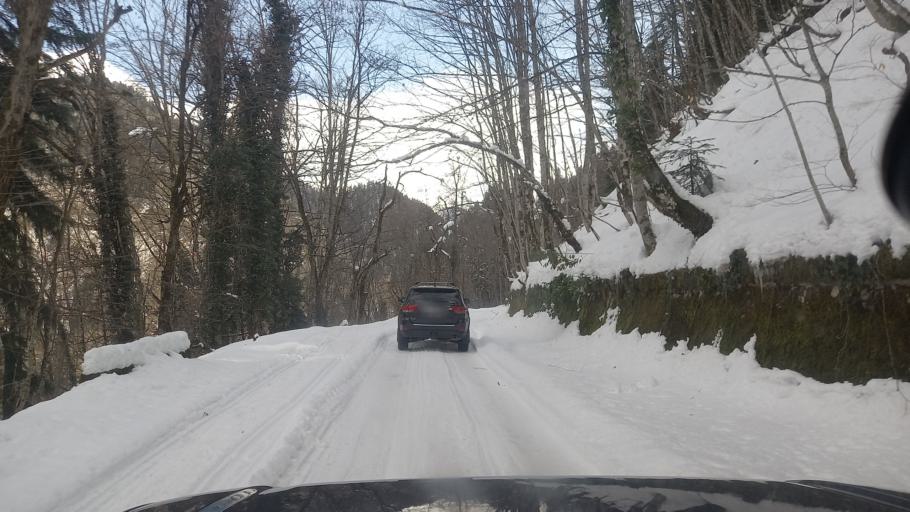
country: GE
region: Abkhazia
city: Gagra
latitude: 43.4781
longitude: 40.5447
